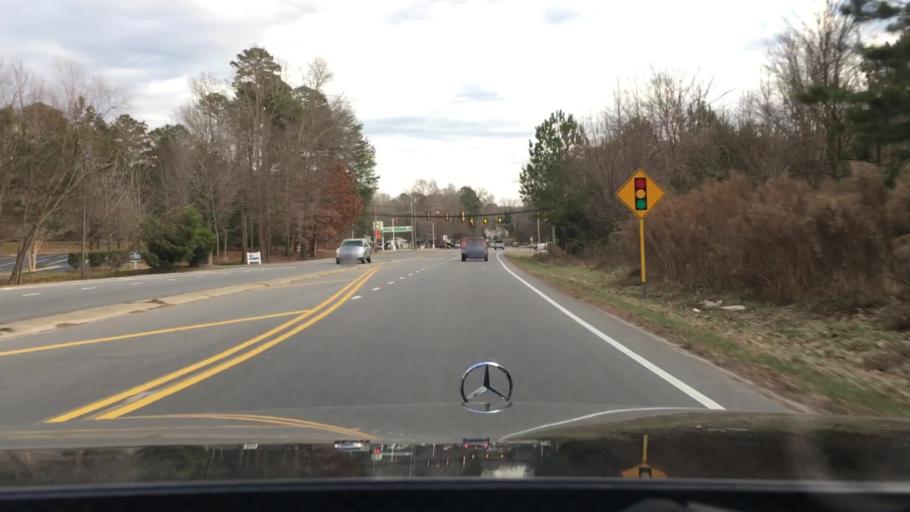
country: US
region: North Carolina
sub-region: Orange County
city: Hillsborough
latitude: 36.0827
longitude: -79.0811
